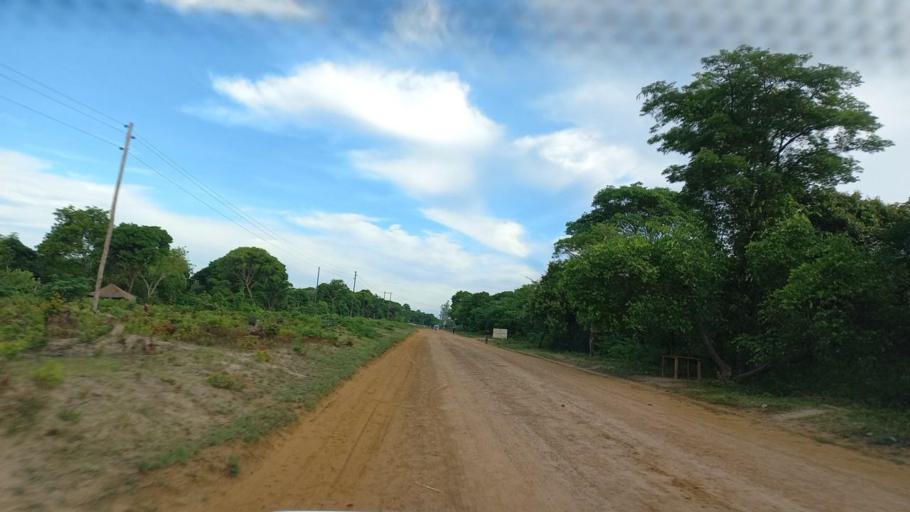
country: ZM
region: North-Western
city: Kabompo
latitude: -13.4055
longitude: 24.3121
